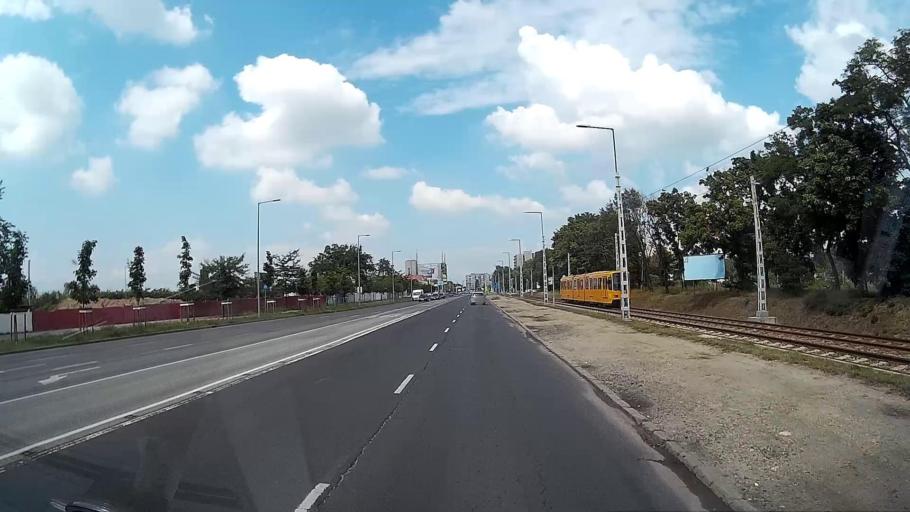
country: HU
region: Budapest
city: Budapest X. keruelet
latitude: 47.4975
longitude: 19.1378
